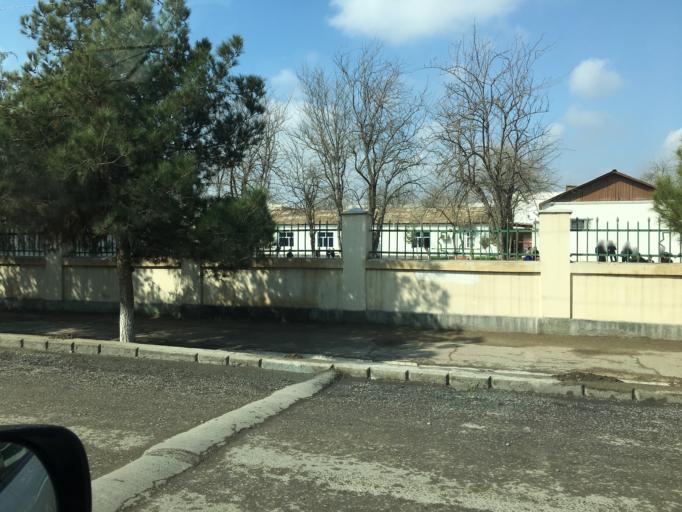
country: TM
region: Mary
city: Mary
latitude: 37.5951
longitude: 61.8293
